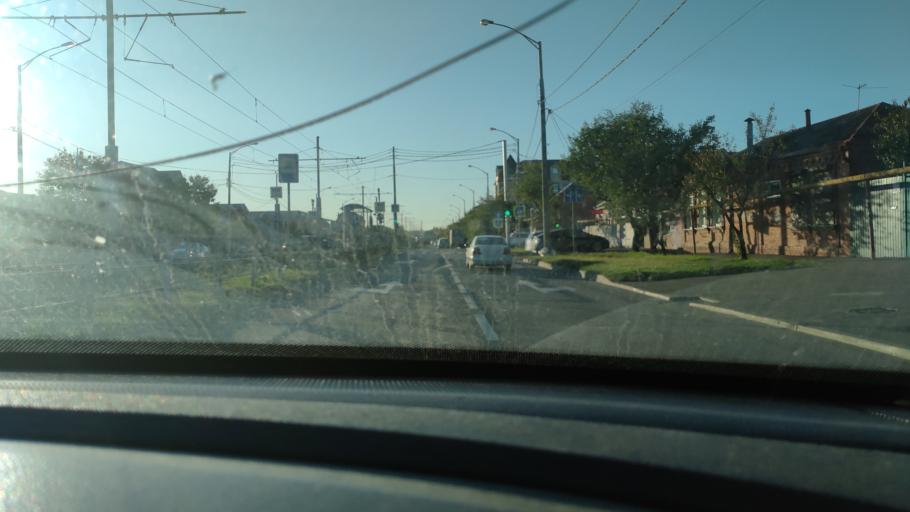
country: RU
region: Krasnodarskiy
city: Krasnodar
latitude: 45.0421
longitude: 38.9440
